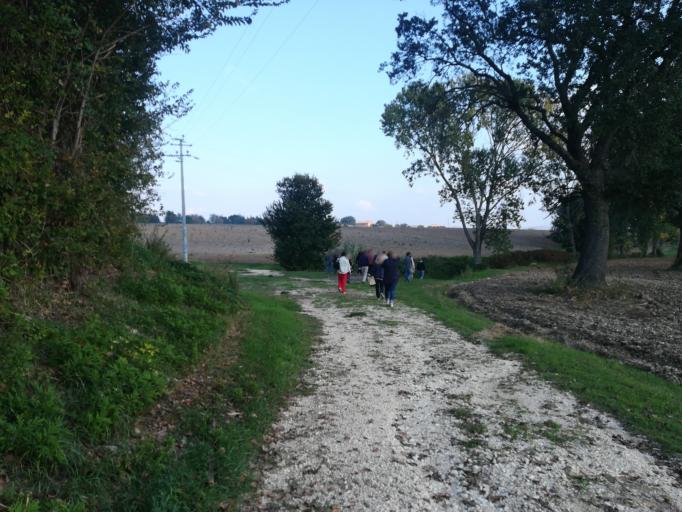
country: IT
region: The Marches
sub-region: Provincia di Macerata
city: Sforzacosta
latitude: 43.2704
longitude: 13.4294
